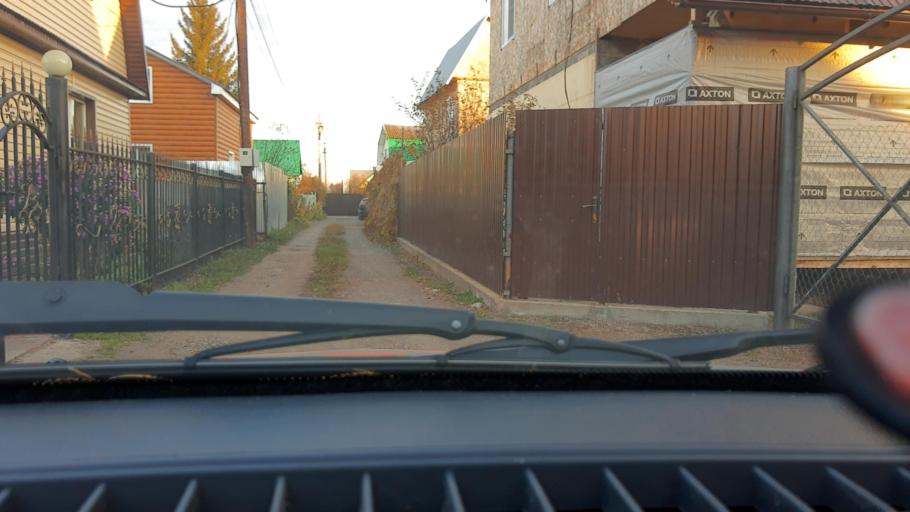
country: RU
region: Bashkortostan
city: Ufa
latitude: 54.6889
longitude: 55.9007
